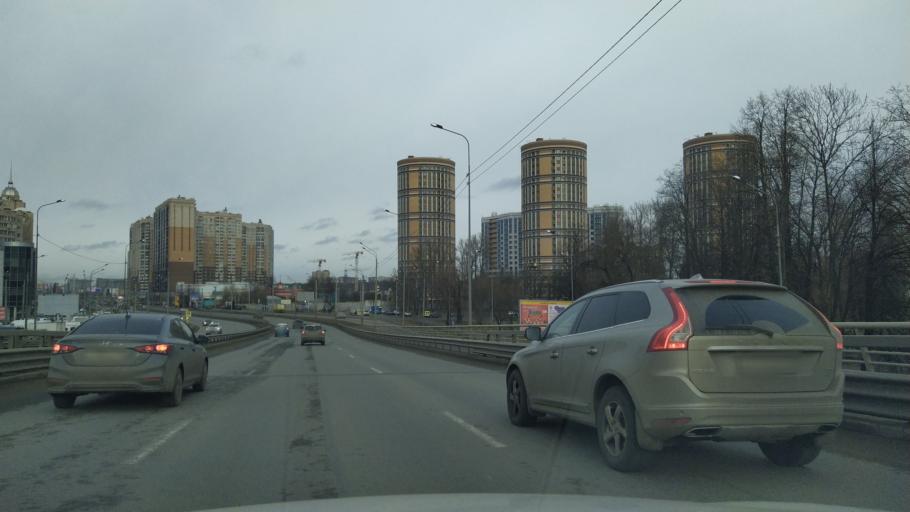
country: RU
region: Leningrad
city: Chernaya Rechka
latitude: 59.9946
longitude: 30.2999
